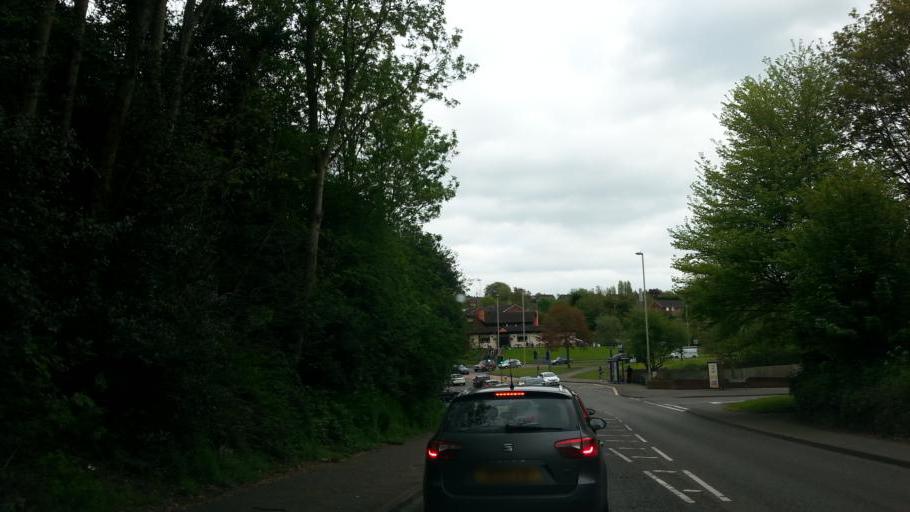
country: GB
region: England
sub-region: Sandwell
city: Cradley Heath
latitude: 52.4551
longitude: -2.0751
